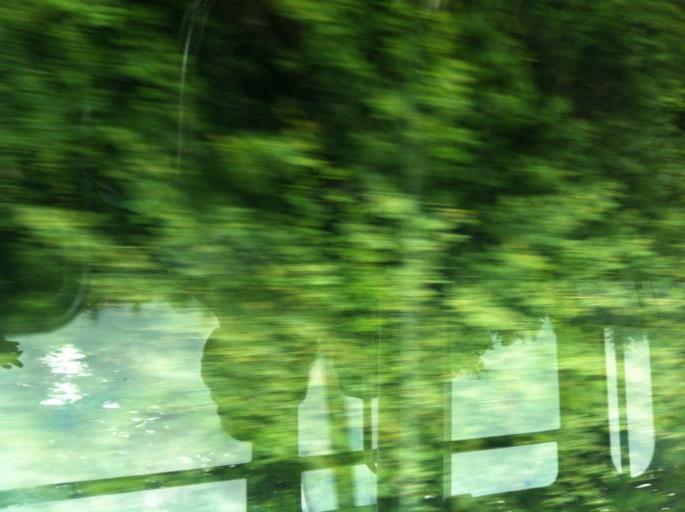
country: DE
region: North Rhine-Westphalia
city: Niederkassel
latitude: 50.7711
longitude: 7.0418
